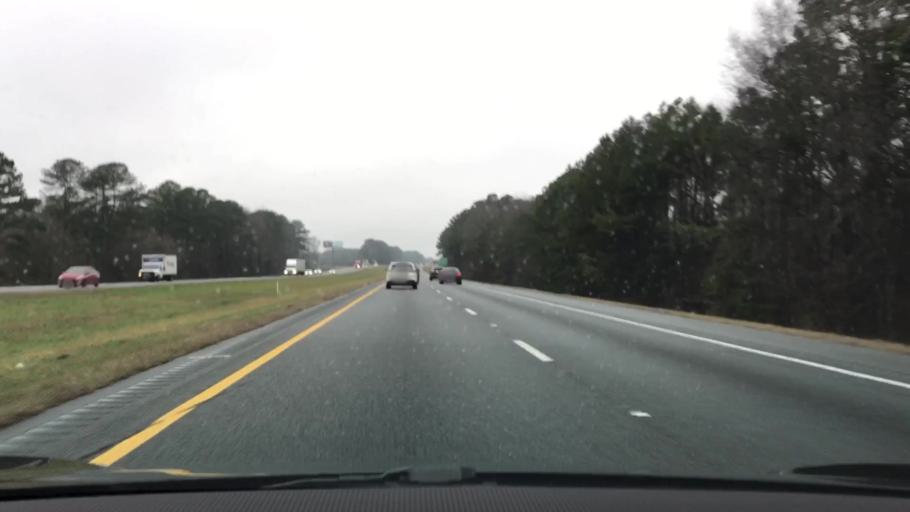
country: US
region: Georgia
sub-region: Walton County
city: Social Circle
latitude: 33.5881
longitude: -83.6143
